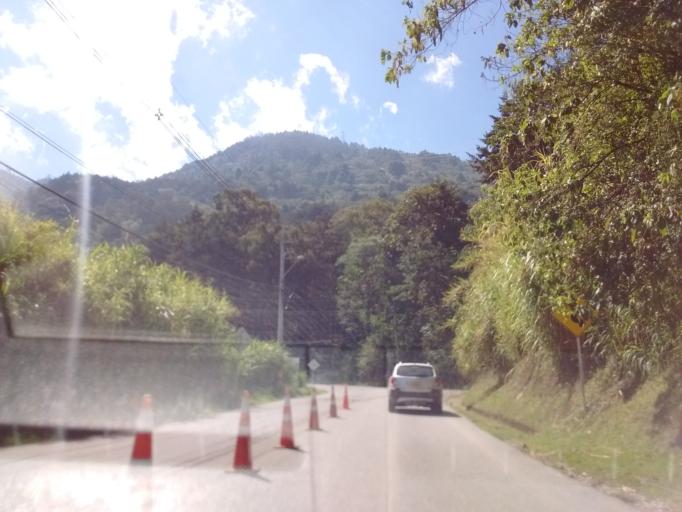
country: CO
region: Antioquia
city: Medellin
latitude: 6.2261
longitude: -75.5158
